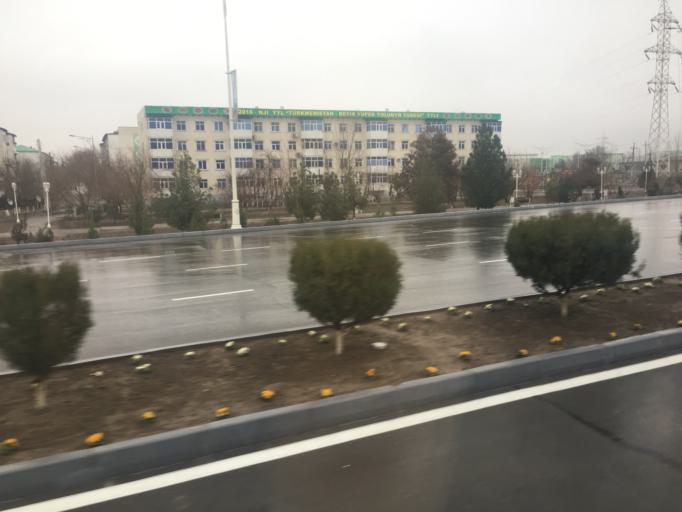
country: TM
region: Lebap
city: Turkmenabat
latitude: 39.0761
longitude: 63.5866
